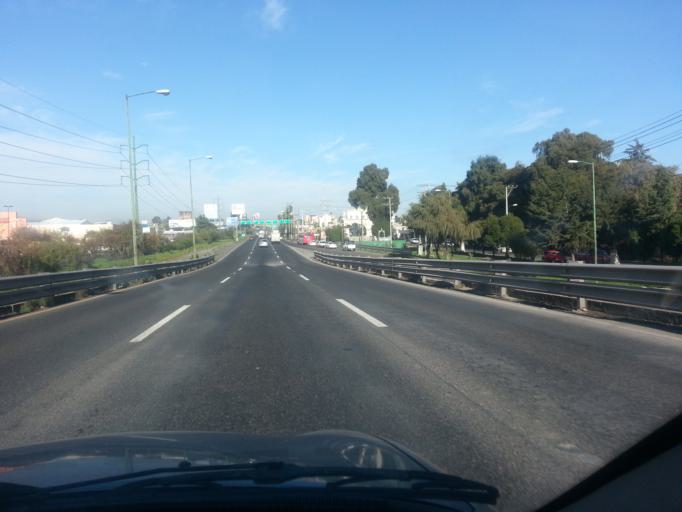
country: MX
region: Mexico
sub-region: Ocoyoacac
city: San Antonio el Llanito
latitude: 19.2843
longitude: -99.4989
